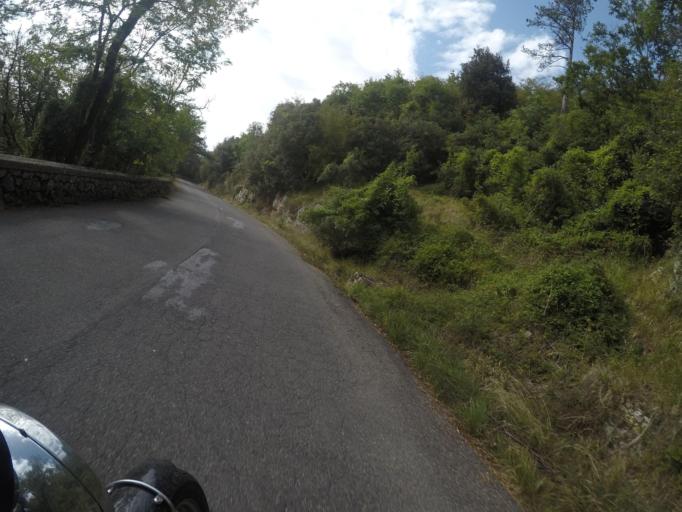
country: IT
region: Tuscany
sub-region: Provincia di Massa-Carrara
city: Fosdinovo
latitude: 44.1207
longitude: 10.0827
